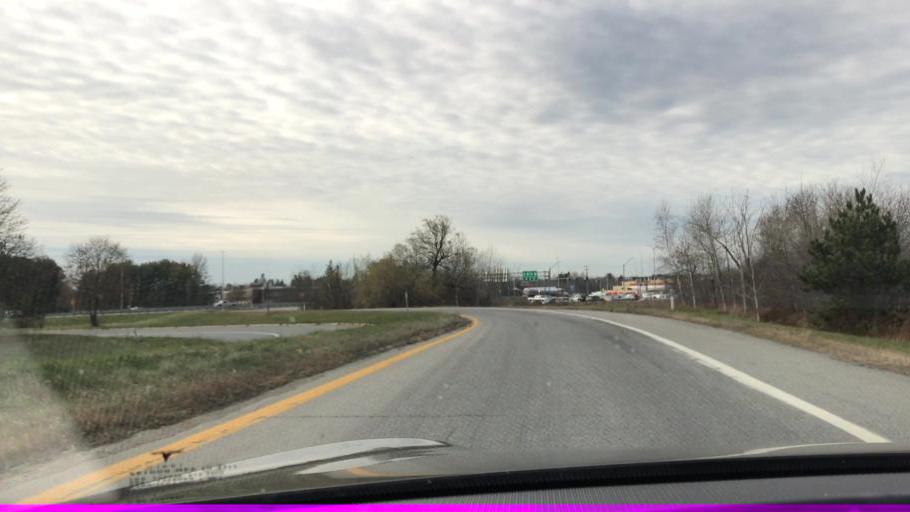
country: US
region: Maine
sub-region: Penobscot County
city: Bangor
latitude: 44.7886
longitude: -68.8093
